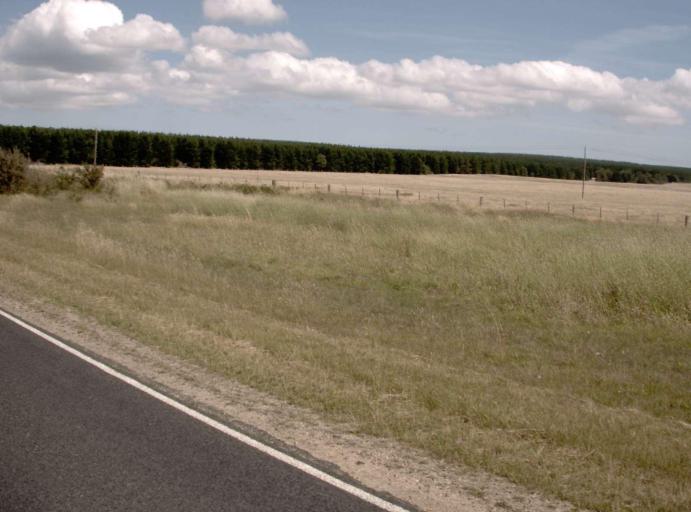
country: AU
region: Victoria
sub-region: Wellington
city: Heyfield
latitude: -38.1580
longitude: 146.8533
